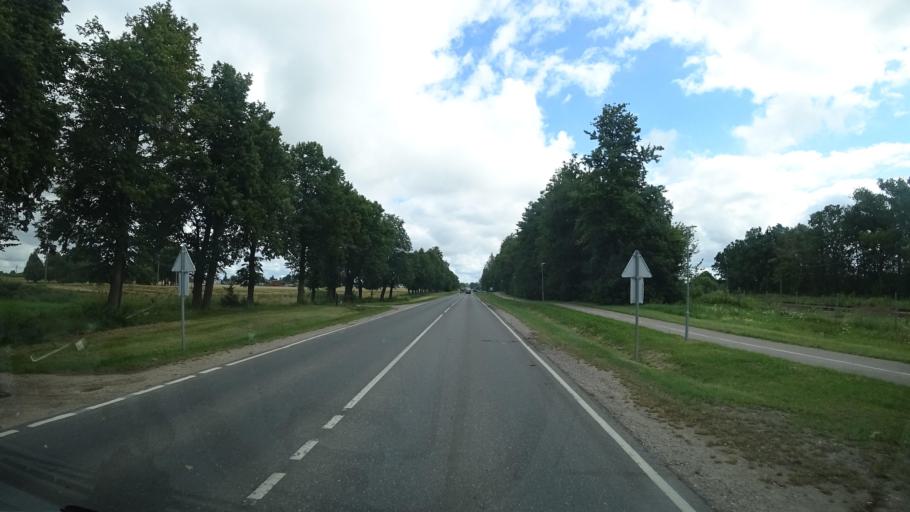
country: LT
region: Marijampoles apskritis
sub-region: Marijampole Municipality
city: Marijampole
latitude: 54.5279
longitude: 23.3275
